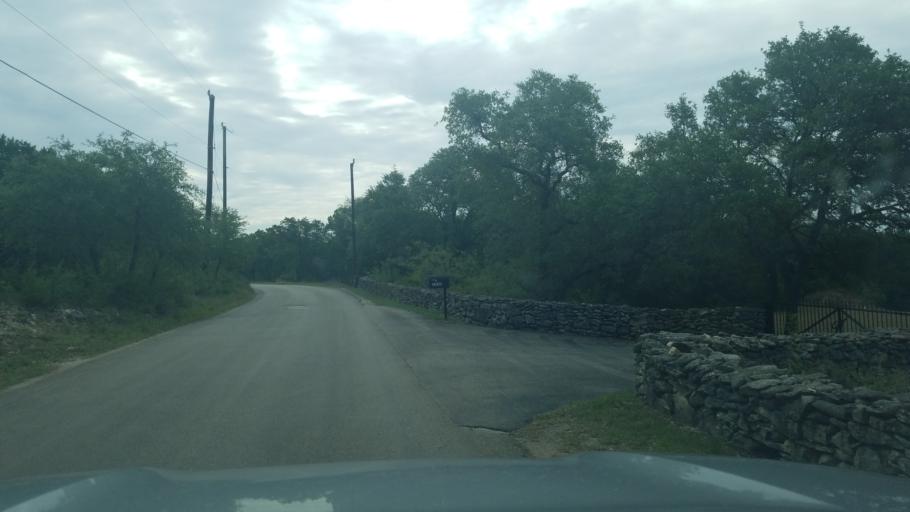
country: US
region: Texas
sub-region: Comal County
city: Bulverde
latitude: 29.7652
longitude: -98.4108
